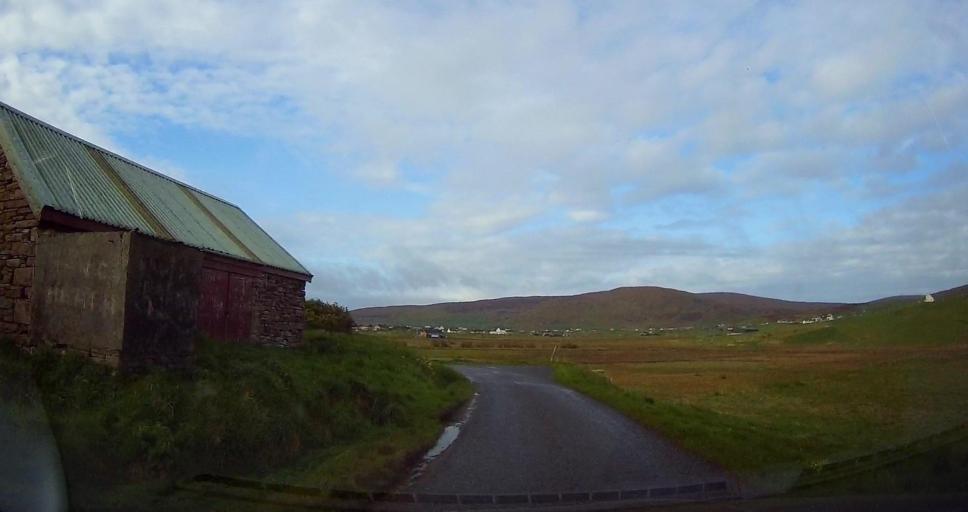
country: GB
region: Scotland
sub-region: Shetland Islands
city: Sandwick
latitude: 60.0499
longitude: -1.2058
